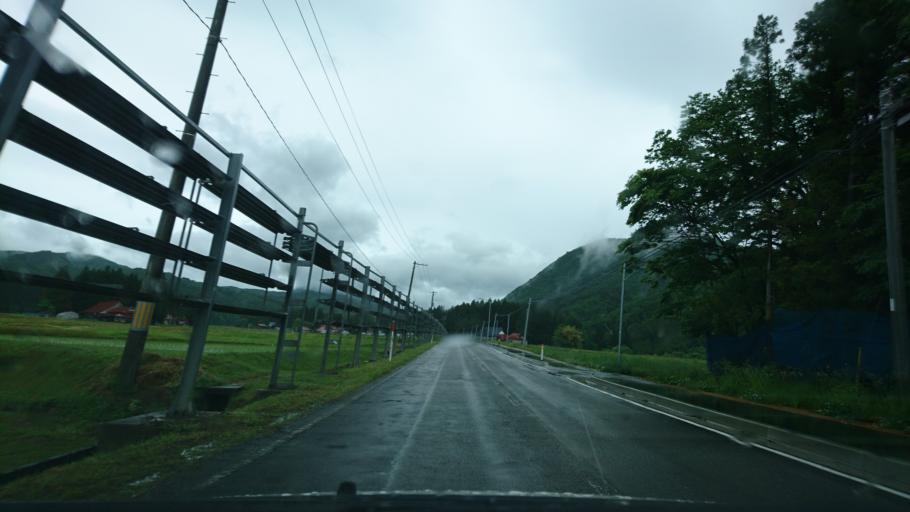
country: JP
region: Iwate
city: Ichinoseki
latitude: 38.9798
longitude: 140.9199
